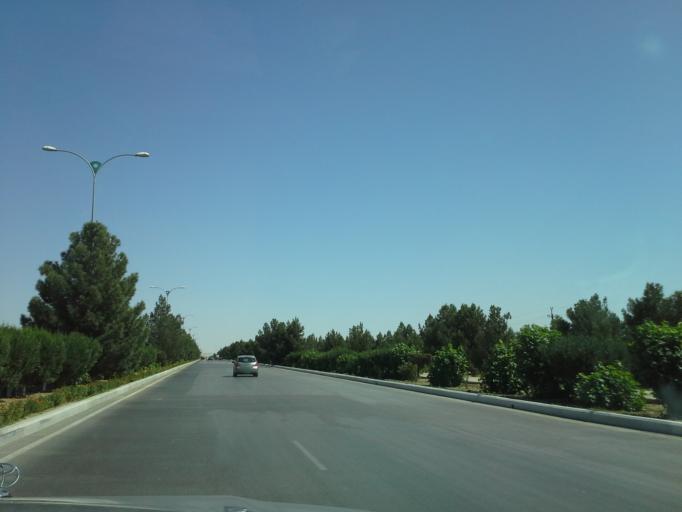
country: TM
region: Ahal
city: Annau
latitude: 37.9185
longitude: 58.4568
